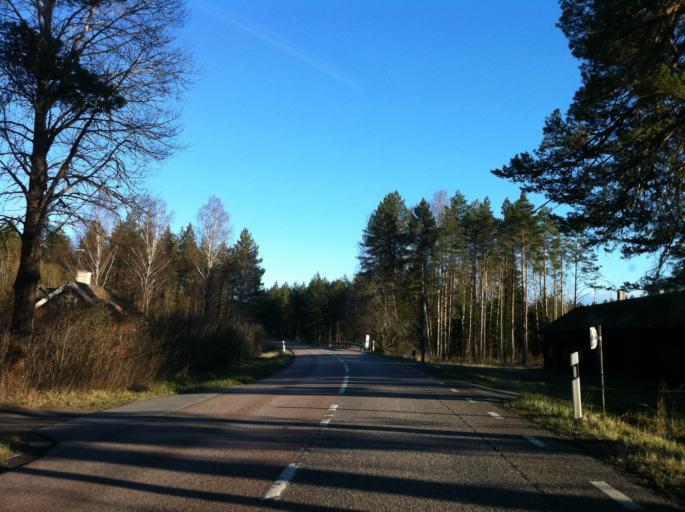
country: SE
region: Uppsala
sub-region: Osthammars Kommun
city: Anneberg
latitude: 60.1687
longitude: 18.4103
